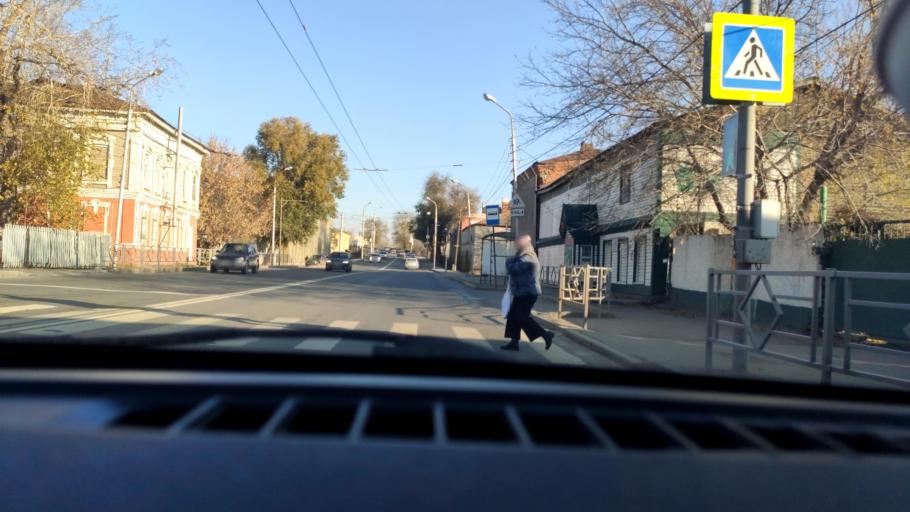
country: RU
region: Samara
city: Rozhdestveno
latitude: 53.1678
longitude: 50.0747
